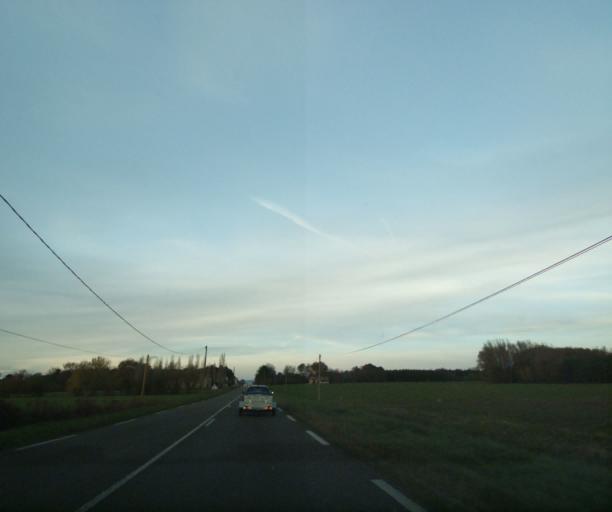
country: FR
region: Aquitaine
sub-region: Departement de la Gironde
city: Langon
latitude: 44.4997
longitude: -0.2378
